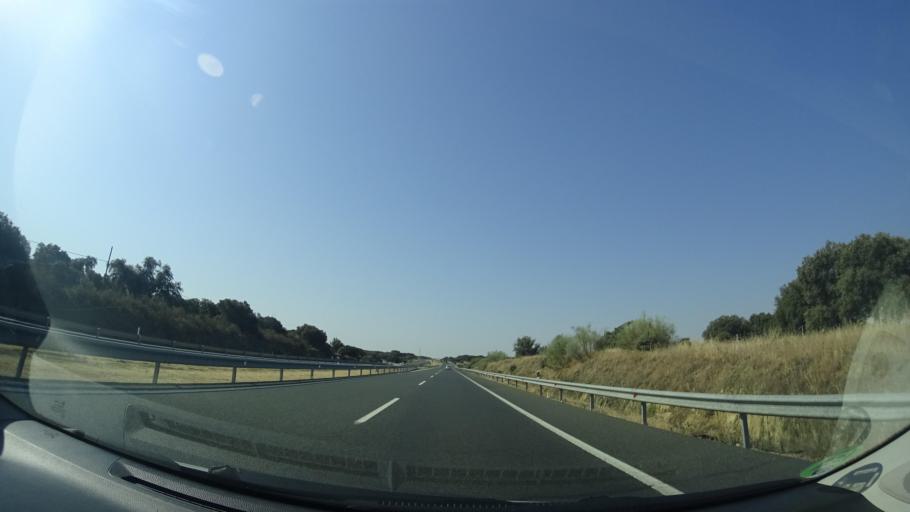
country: ES
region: Extremadura
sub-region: Provincia de Caceres
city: Torrecillas de la Tiesa
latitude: 39.5456
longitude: -5.8273
